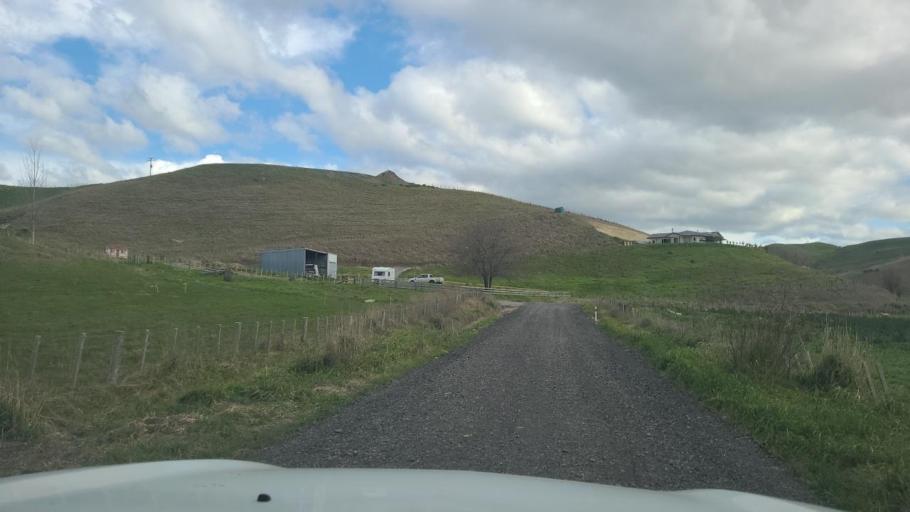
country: NZ
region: Hawke's Bay
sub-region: Hastings District
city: Hastings
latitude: -39.6615
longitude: 176.6520
